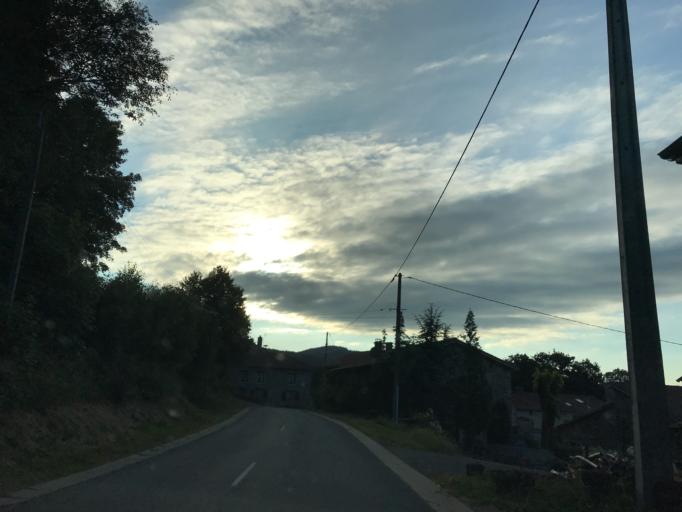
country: FR
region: Rhone-Alpes
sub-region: Departement de la Loire
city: Sail-sous-Couzan
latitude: 45.7450
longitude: 3.8539
